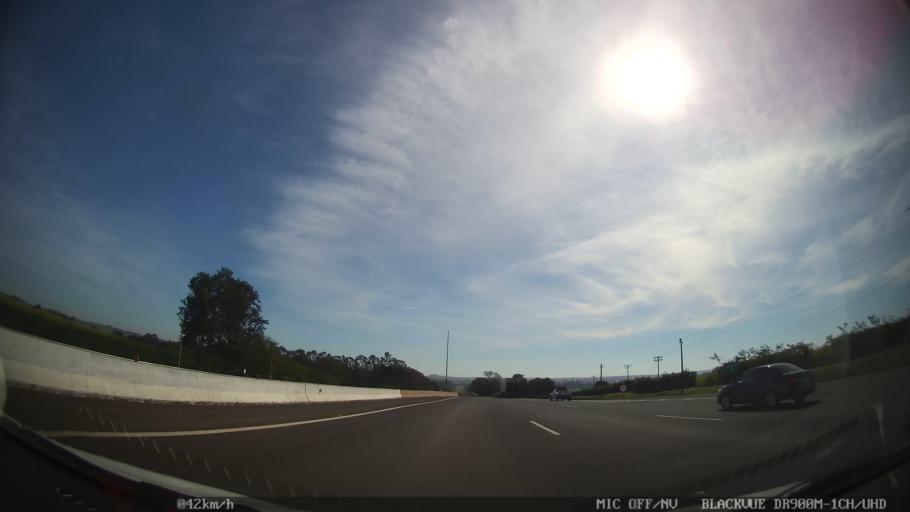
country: BR
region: Sao Paulo
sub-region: Leme
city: Leme
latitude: -22.2482
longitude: -47.3901
